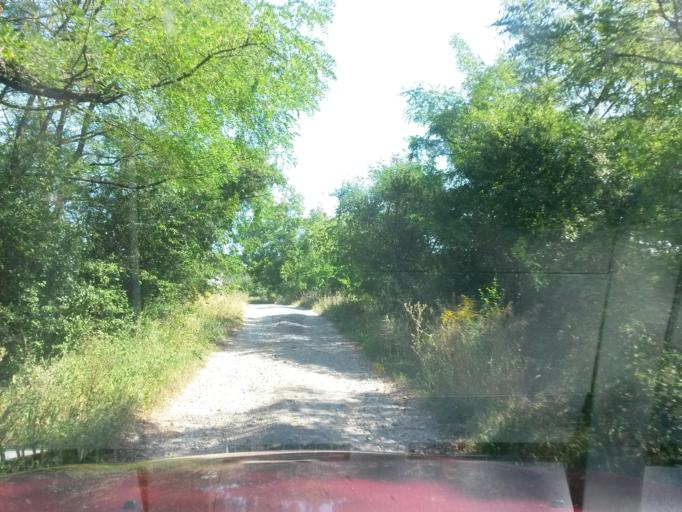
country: HU
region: Borsod-Abauj-Zemplen
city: Gonc
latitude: 48.5283
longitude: 21.1910
